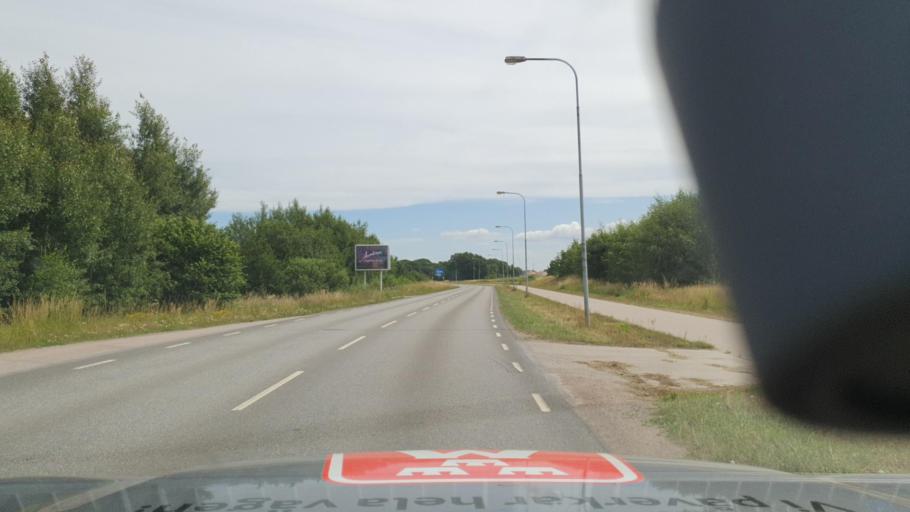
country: SE
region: Kalmar
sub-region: Kalmar Kommun
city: Rinkabyholm
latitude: 56.6734
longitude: 16.2967
